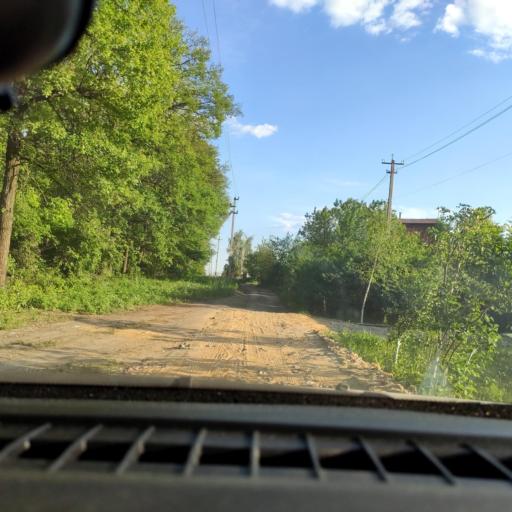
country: RU
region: Voronezj
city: Maslovka
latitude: 51.5207
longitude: 39.2387
